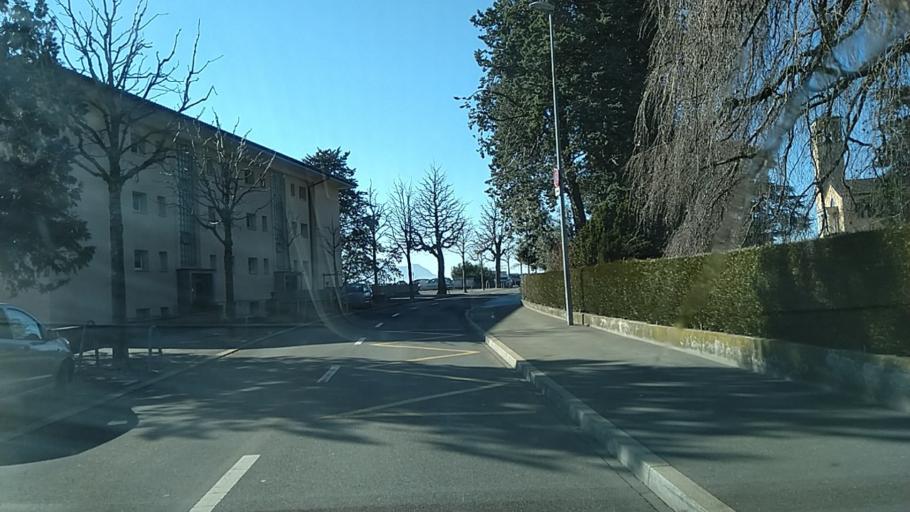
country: CH
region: Vaud
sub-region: Riviera-Pays-d'Enhaut District
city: Le Chatelard
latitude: 46.4428
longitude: 6.8993
